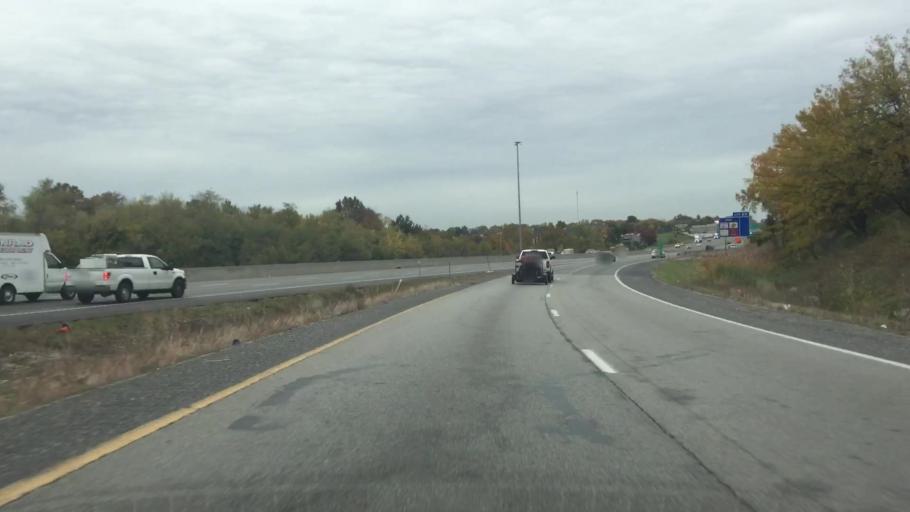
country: US
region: Missouri
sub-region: Jackson County
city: Raytown
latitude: 39.0217
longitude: -94.5004
